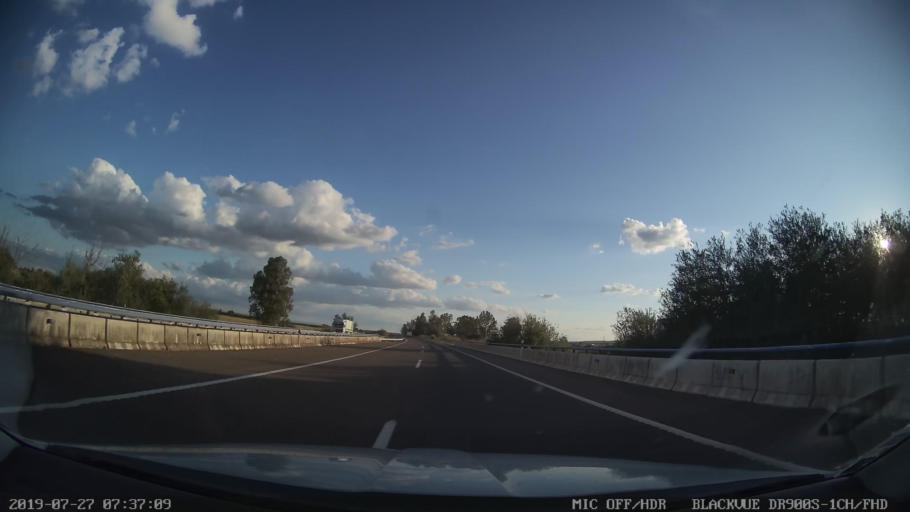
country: ES
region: Extremadura
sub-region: Provincia de Badajoz
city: Santa Amalia
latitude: 39.0942
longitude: -6.0151
